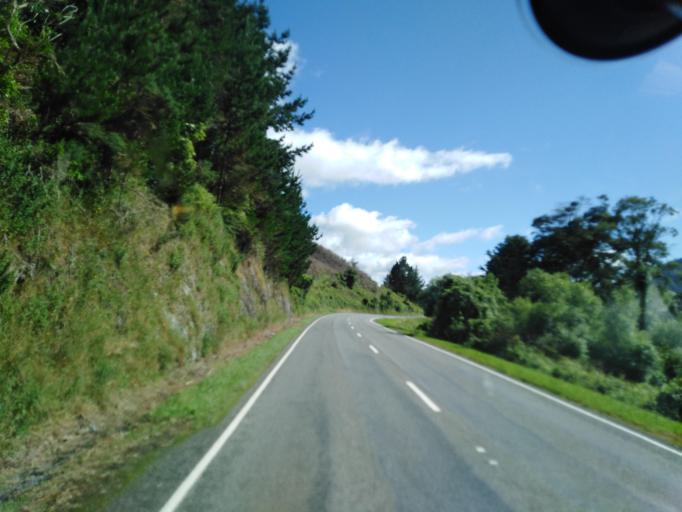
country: NZ
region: Nelson
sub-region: Nelson City
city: Nelson
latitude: -41.2564
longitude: 173.5761
